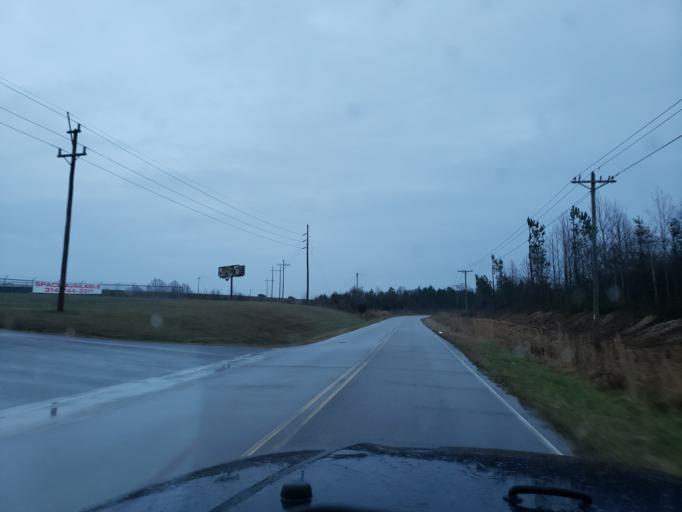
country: US
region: South Carolina
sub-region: Cherokee County
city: Blacksburg
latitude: 35.1576
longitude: -81.4683
